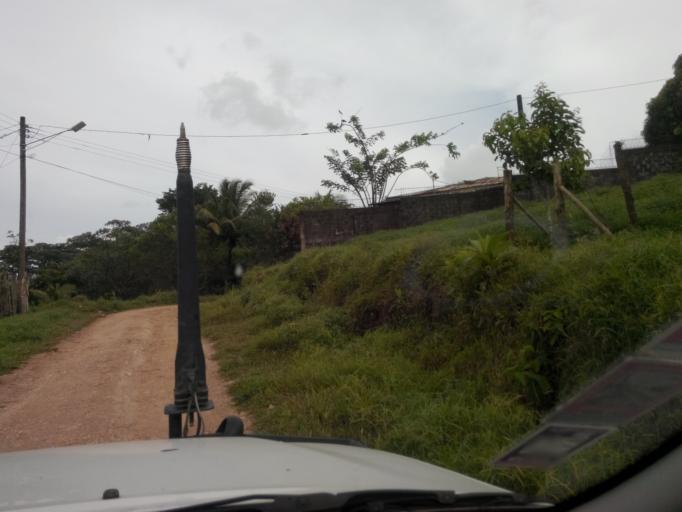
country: NI
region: Atlantico Sur
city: Bluefields
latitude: 12.0285
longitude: -83.7737
